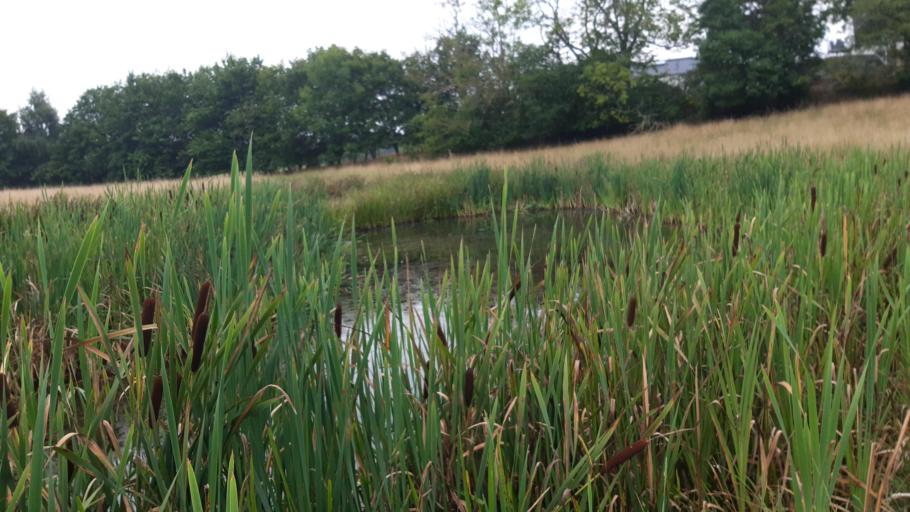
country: DK
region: Capital Region
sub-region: Ballerup Kommune
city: Malov
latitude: 55.7351
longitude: 12.3343
